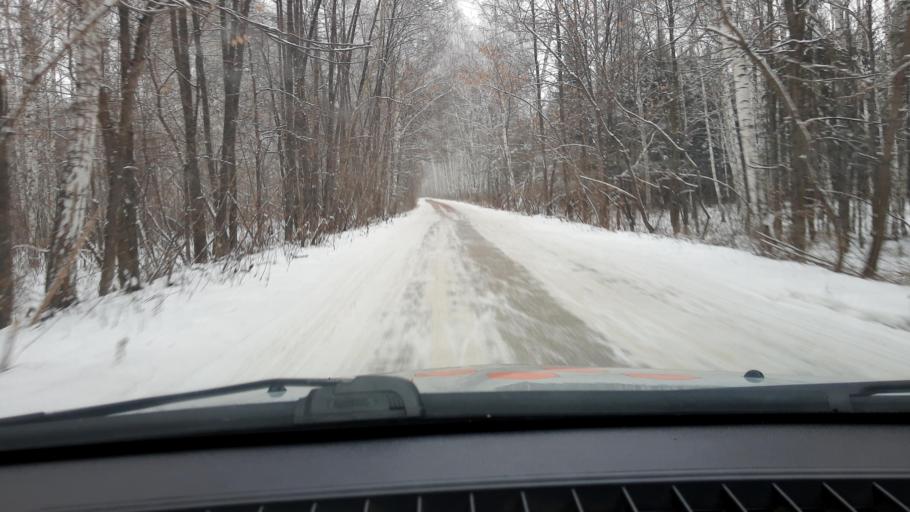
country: RU
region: Bashkortostan
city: Iglino
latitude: 54.8211
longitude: 56.1911
